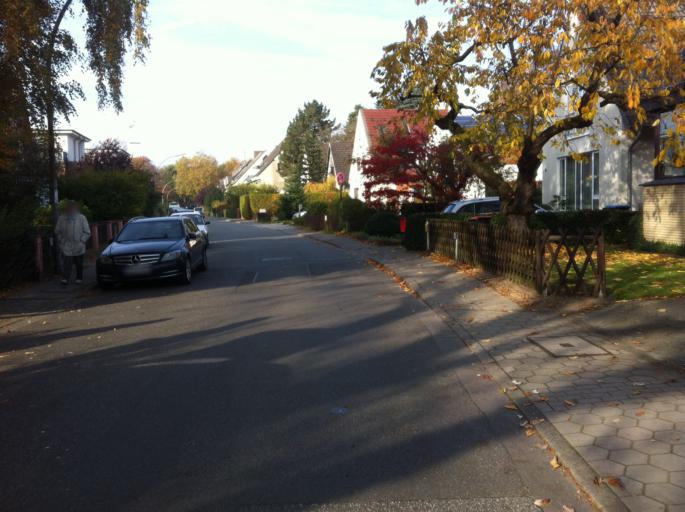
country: DE
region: Hamburg
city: Altona
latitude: 53.5716
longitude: 9.9364
